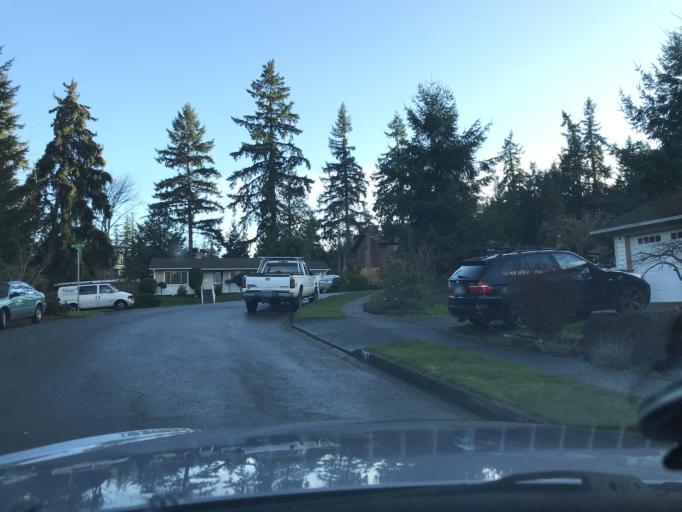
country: US
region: Washington
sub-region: King County
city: Sammamish
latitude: 47.6393
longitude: -122.1020
